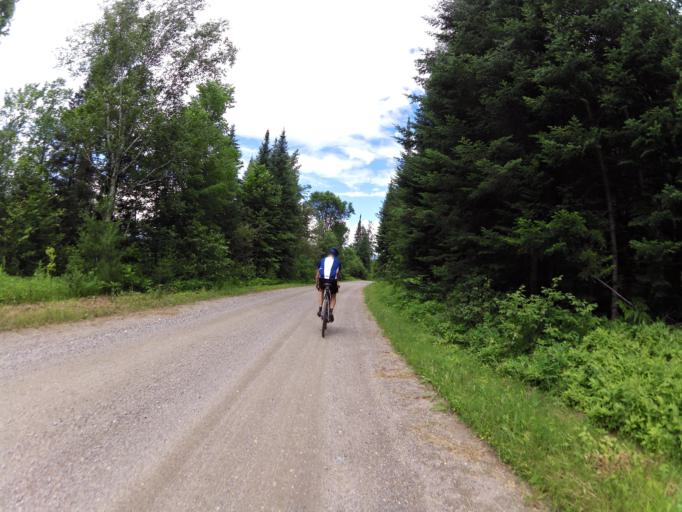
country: CA
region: Ontario
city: Renfrew
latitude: 45.1278
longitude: -76.6851
